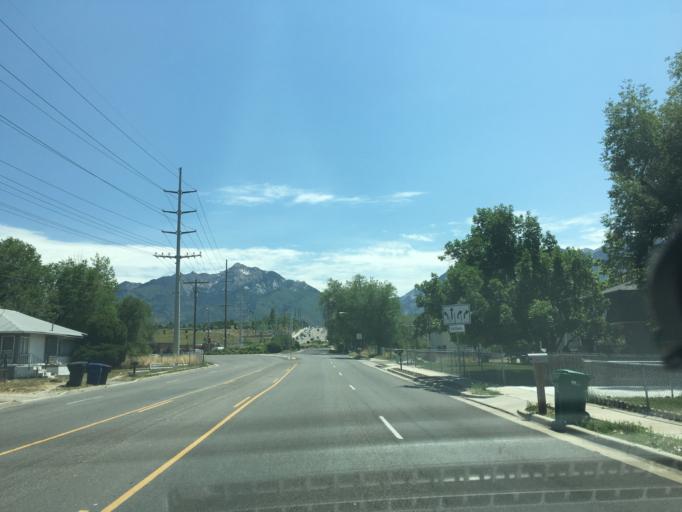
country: US
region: Utah
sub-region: Salt Lake County
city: Sandy Hills
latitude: 40.5805
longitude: -111.8633
